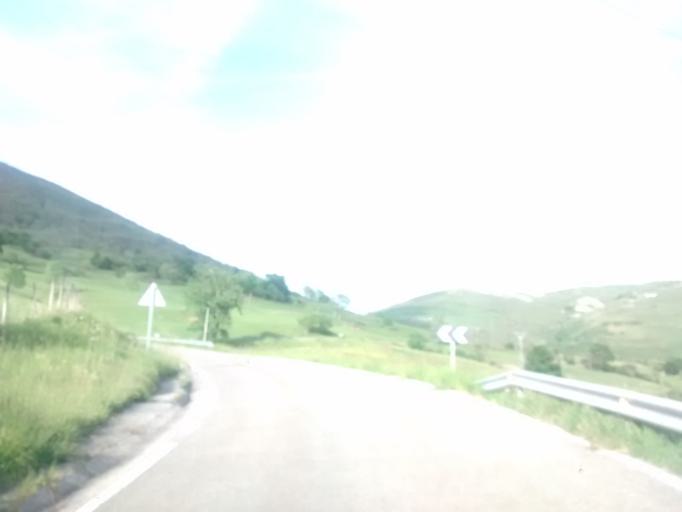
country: ES
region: Cantabria
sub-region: Provincia de Cantabria
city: Potes
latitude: 43.2412
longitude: -4.5603
